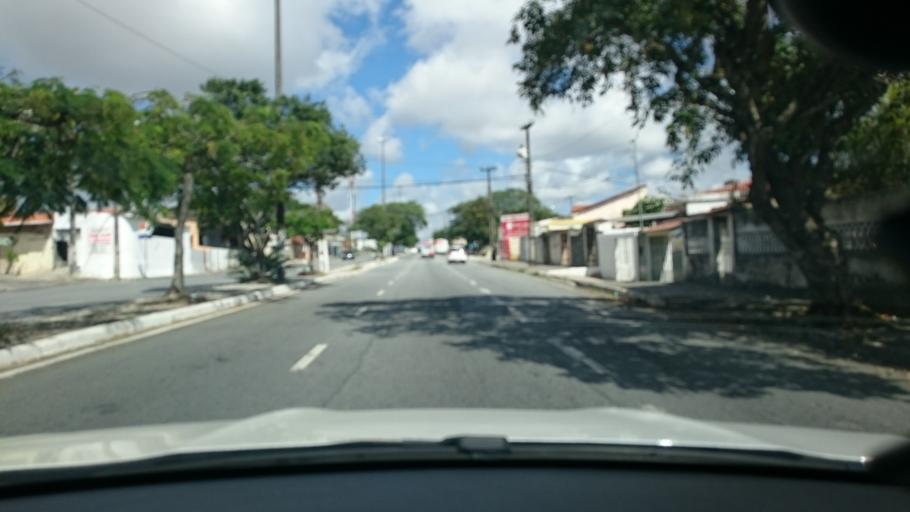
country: BR
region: Paraiba
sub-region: Campina Grande
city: Campina Grande
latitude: -7.2240
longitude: -35.8937
